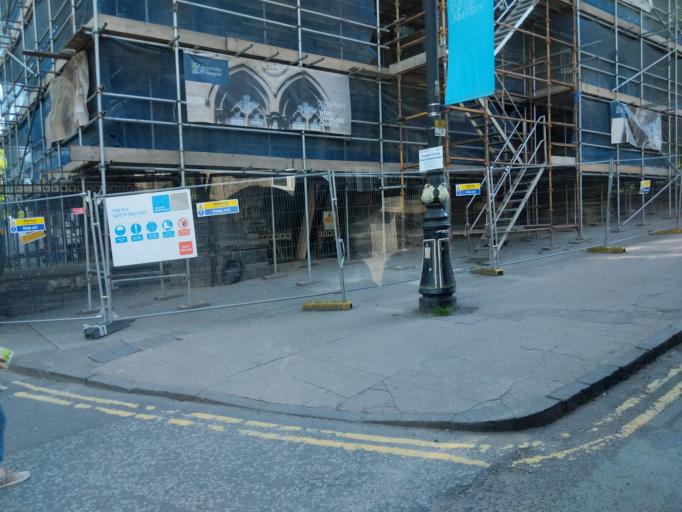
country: GB
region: Scotland
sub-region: Glasgow City
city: Glasgow
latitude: 55.8720
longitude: -4.2856
